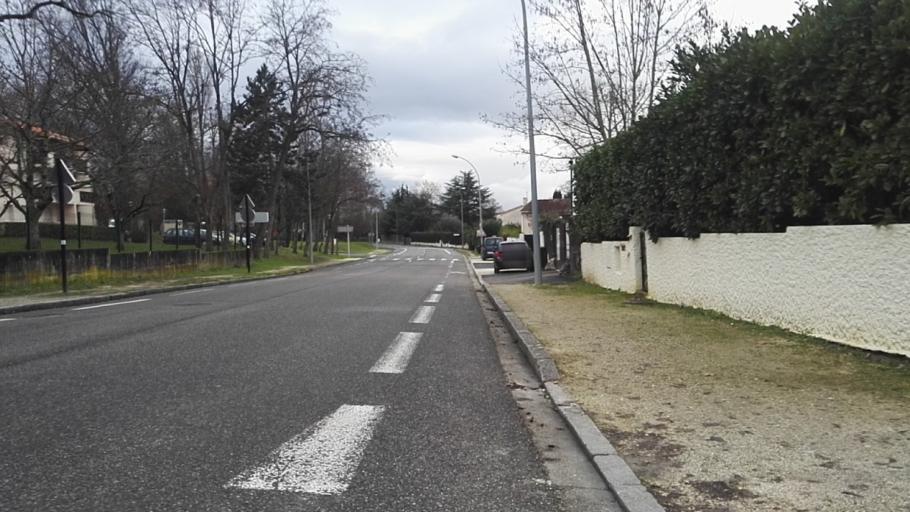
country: FR
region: Aquitaine
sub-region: Departement de la Gironde
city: Bruges
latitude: 44.8640
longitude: -0.6308
